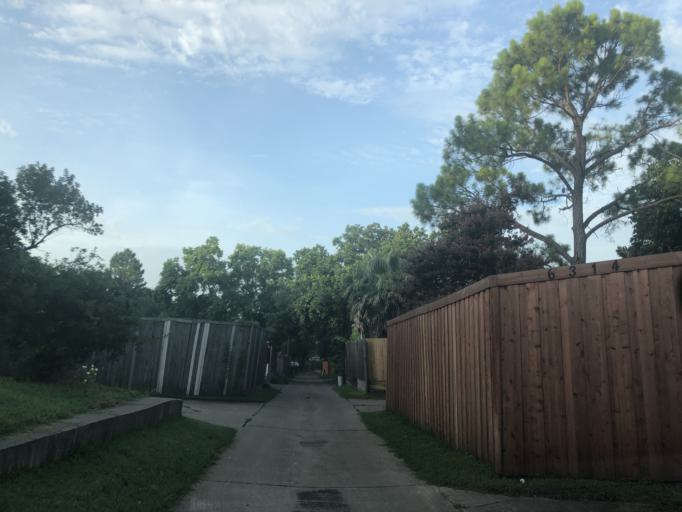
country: US
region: Texas
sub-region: Dallas County
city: Sunnyvale
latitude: 32.8376
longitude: -96.5900
